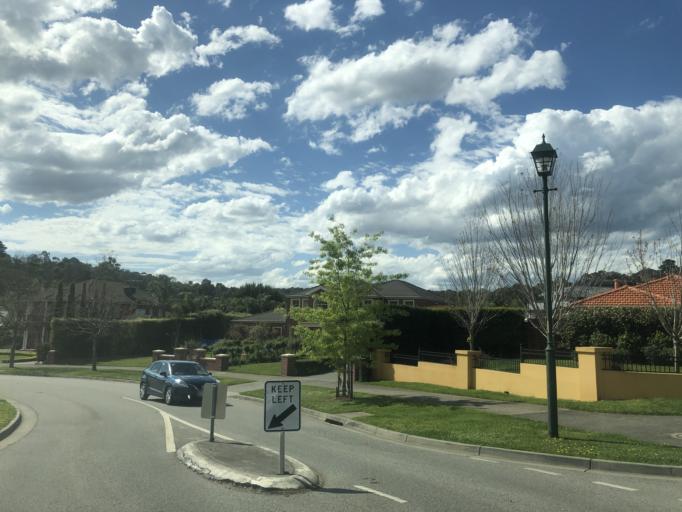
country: AU
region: Victoria
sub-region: Casey
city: Endeavour Hills
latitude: -37.9584
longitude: 145.2790
